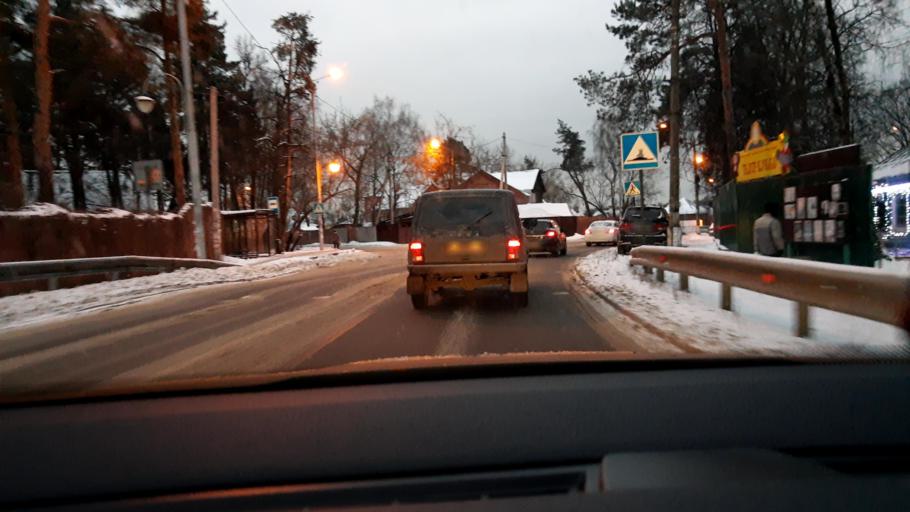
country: RU
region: Moskovskaya
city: Tomilino
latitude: 55.6487
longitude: 37.9557
